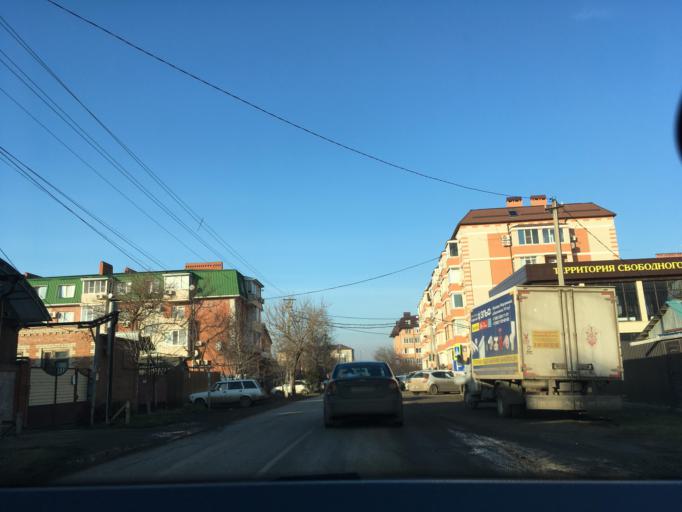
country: RU
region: Krasnodarskiy
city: Krasnodar
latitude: 45.0728
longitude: 39.0213
